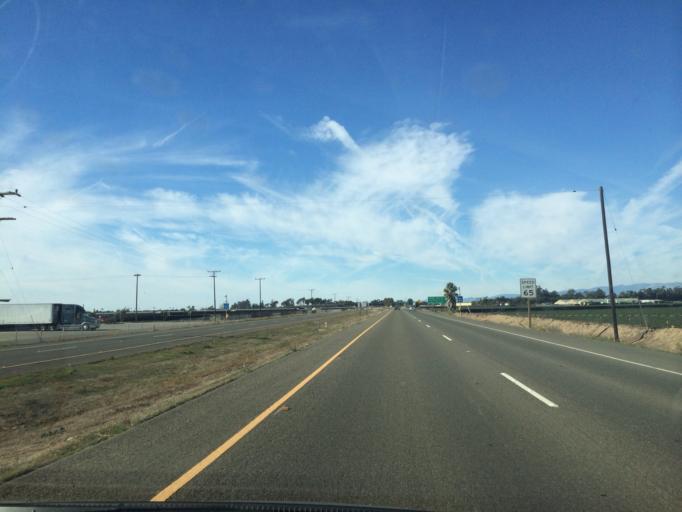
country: US
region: California
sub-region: Ventura County
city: Oxnard
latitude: 34.1561
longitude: -119.1269
